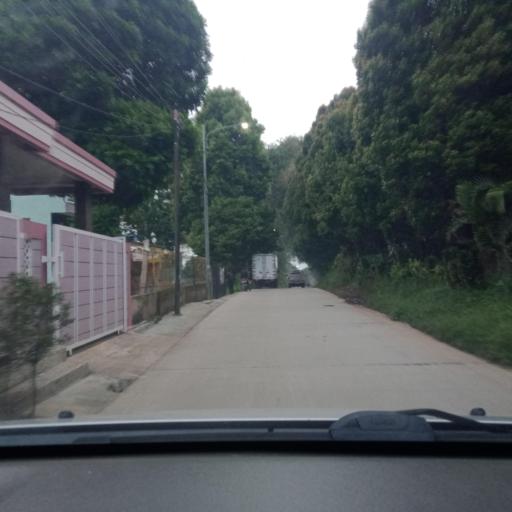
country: ID
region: West Java
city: Lembang
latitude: -6.8296
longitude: 107.5859
